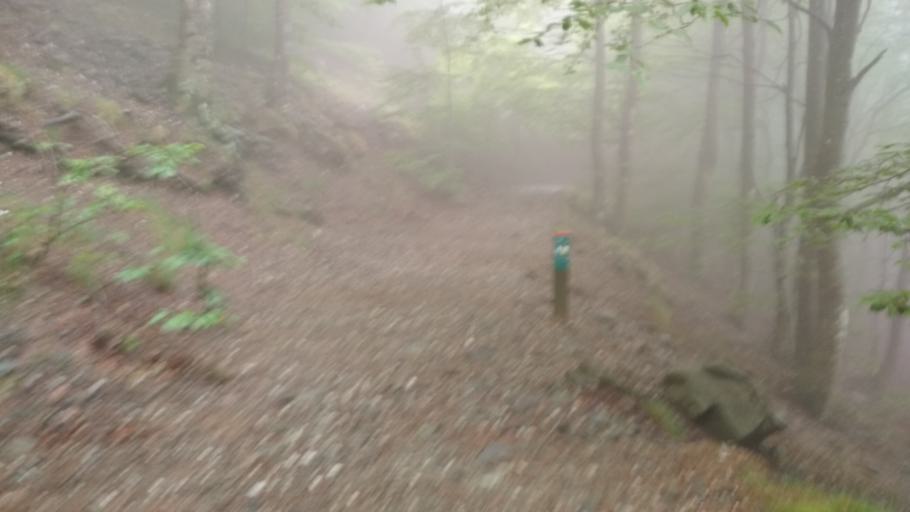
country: ES
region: Catalonia
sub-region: Provincia de Barcelona
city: Fogars de Montclus
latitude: 41.7743
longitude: 2.4449
